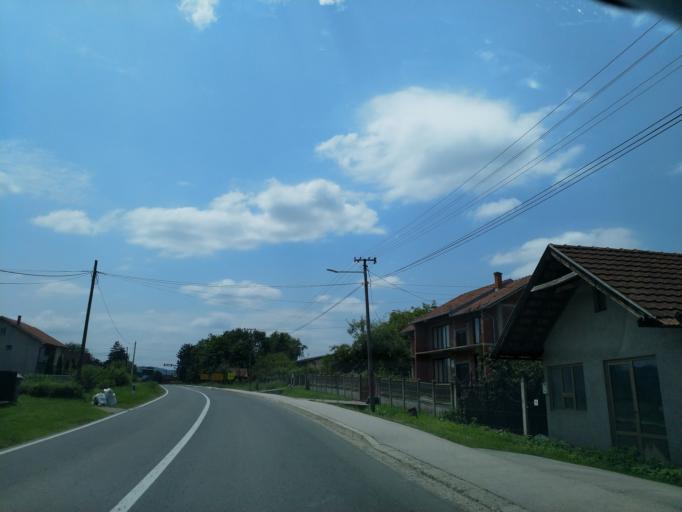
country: RS
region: Central Serbia
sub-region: Toplicki Okrug
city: Blace
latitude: 43.4483
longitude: 21.2329
